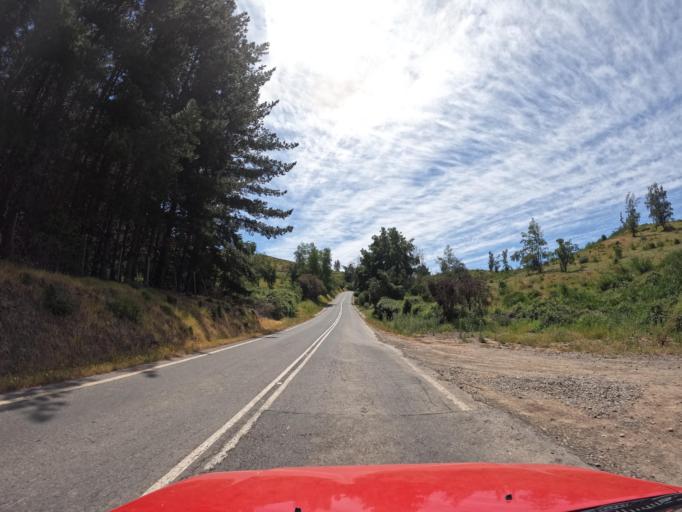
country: CL
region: Maule
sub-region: Provincia de Talca
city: Talca
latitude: -35.0670
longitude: -71.7339
